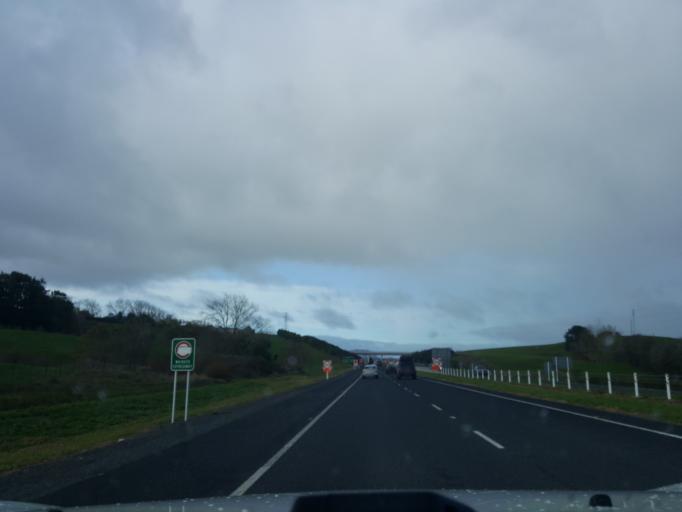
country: NZ
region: Waikato
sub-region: Waikato District
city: Ngaruawahia
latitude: -37.6280
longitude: 175.2063
